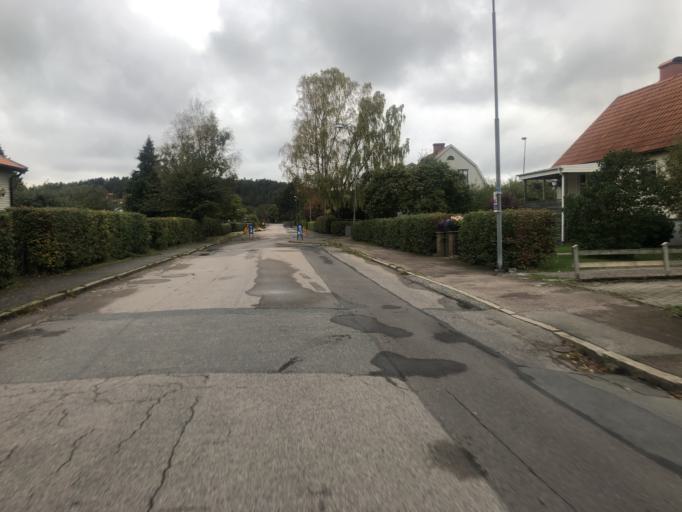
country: SE
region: Vaestra Goetaland
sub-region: Molndal
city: Moelndal
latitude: 57.6527
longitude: 11.9961
